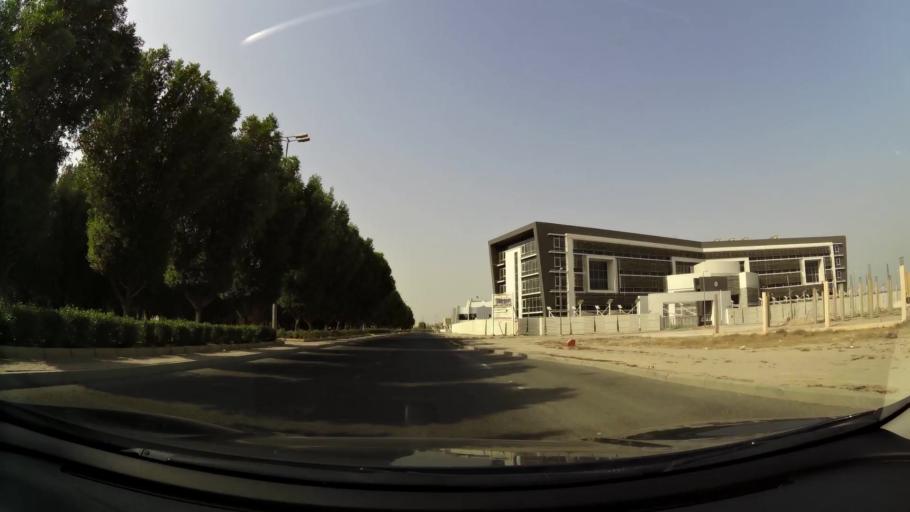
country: KW
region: Mubarak al Kabir
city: Sabah as Salim
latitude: 29.2685
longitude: 48.0521
